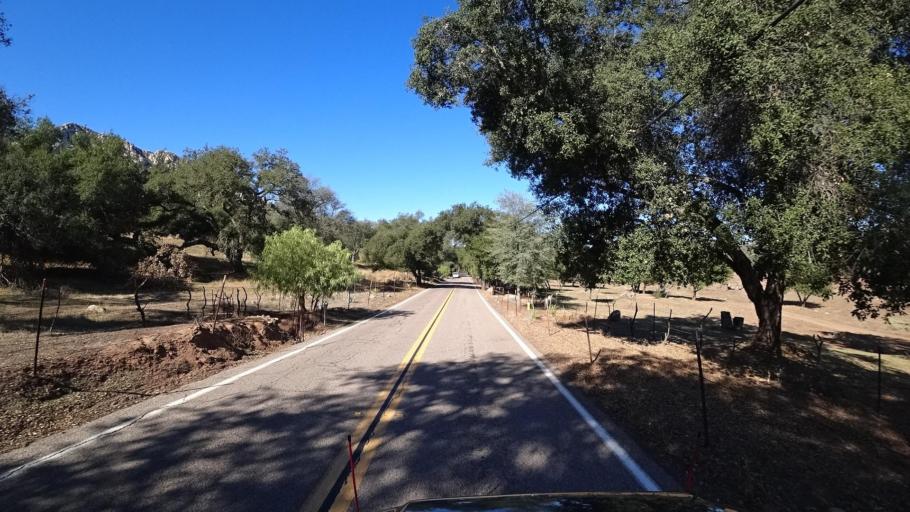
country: US
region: California
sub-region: San Diego County
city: Alpine
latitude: 32.7129
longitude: -116.7508
